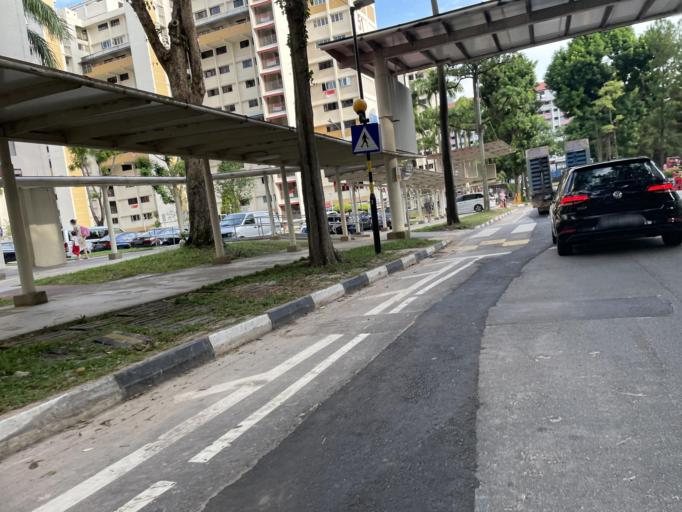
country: SG
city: Singapore
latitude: 1.2742
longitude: 103.8094
